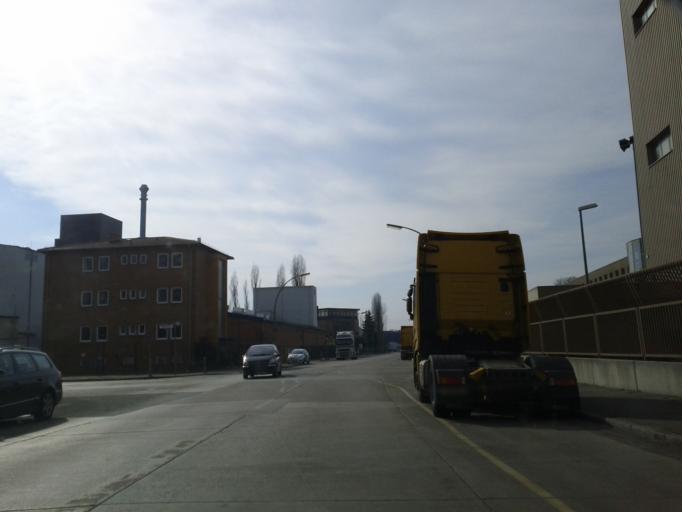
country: DE
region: Berlin
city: Plaenterwald
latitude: 52.4637
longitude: 13.4638
